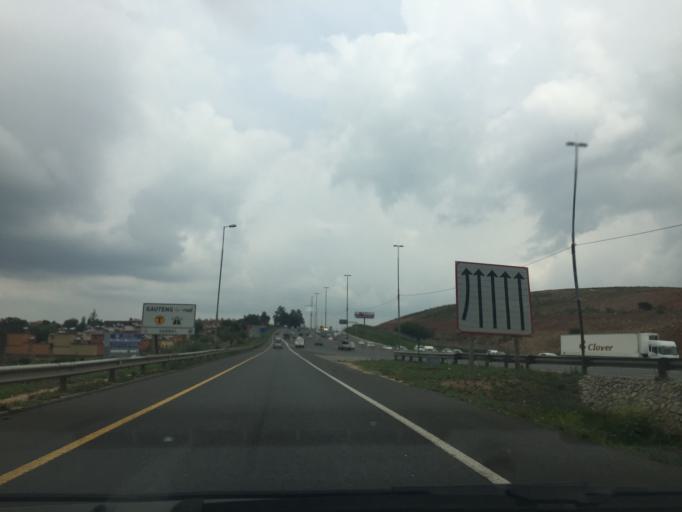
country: ZA
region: Gauteng
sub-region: City of Johannesburg Metropolitan Municipality
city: Modderfontein
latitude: -26.1008
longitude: 28.1214
